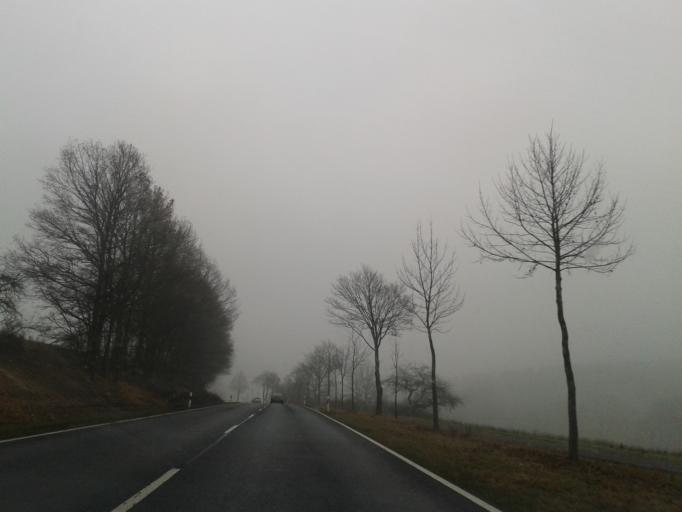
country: DE
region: Bavaria
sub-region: Upper Franconia
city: Sesslach
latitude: 50.2273
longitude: 10.8484
